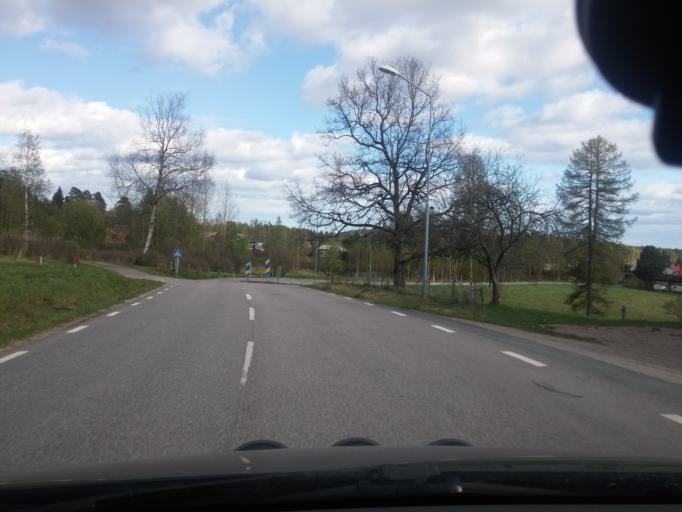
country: SE
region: Gaevleborg
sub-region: Bollnas Kommun
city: Arbra
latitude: 61.4779
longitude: 16.3780
